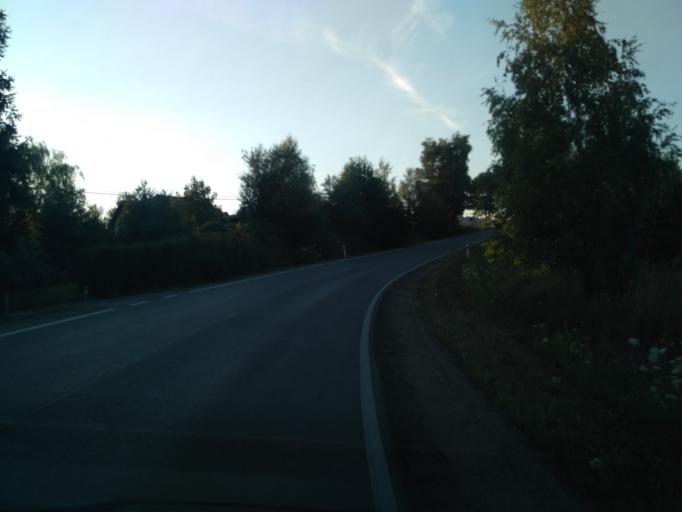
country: PL
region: Subcarpathian Voivodeship
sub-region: Powiat krosnienski
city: Korczyna
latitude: 49.7227
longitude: 21.8093
